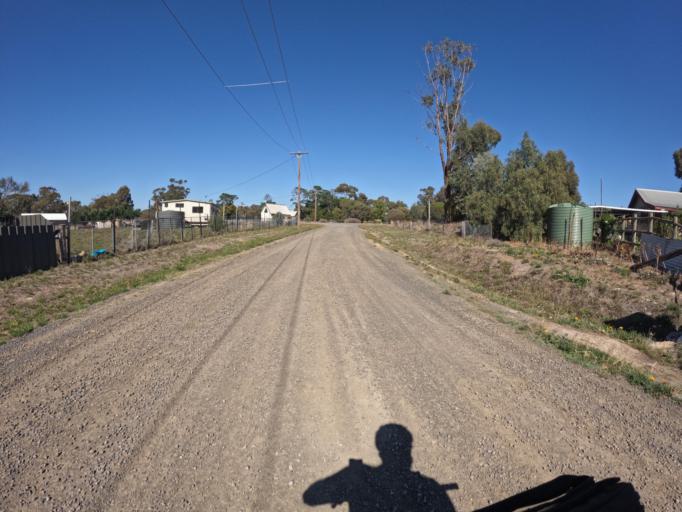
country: AU
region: Victoria
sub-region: Greater Bendigo
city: Kennington
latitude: -36.8265
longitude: 144.5849
